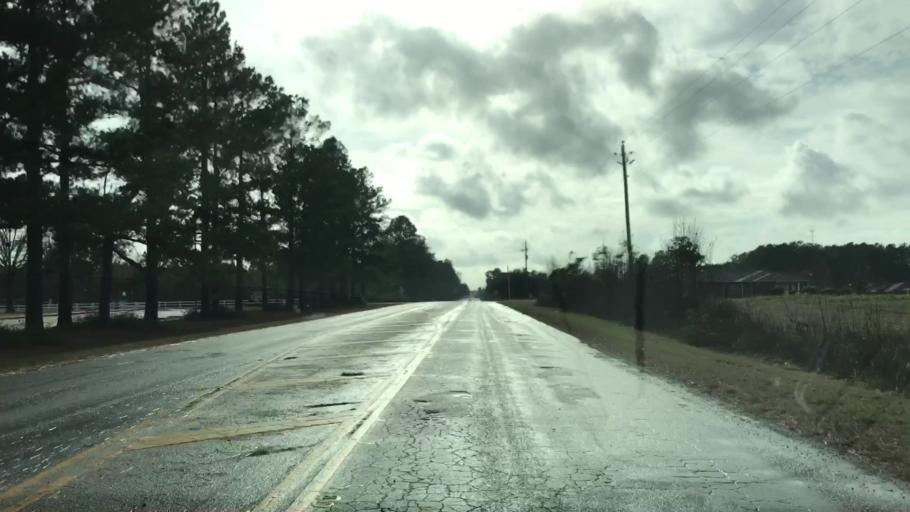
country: US
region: South Carolina
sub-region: Williamsburg County
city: Andrews
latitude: 33.4638
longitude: -79.5696
